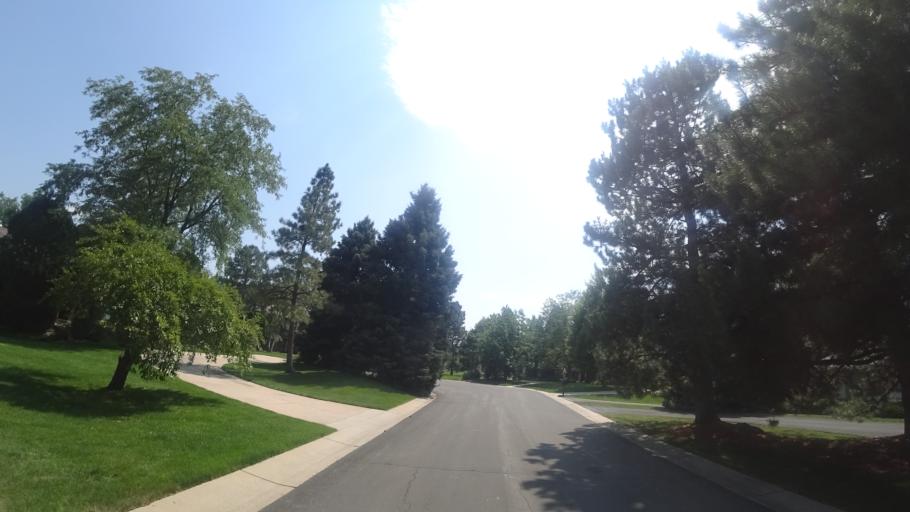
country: US
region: Colorado
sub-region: Arapahoe County
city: Greenwood Village
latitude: 39.6197
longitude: -104.9667
